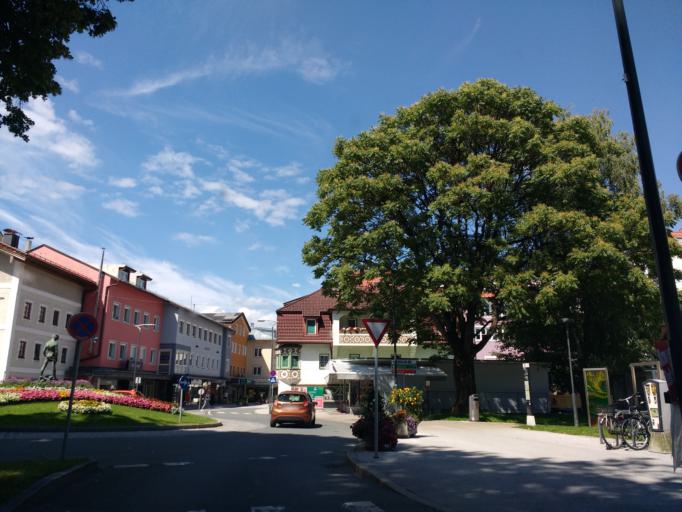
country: AT
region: Tyrol
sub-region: Politischer Bezirk Kufstein
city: Kufstein
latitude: 47.5842
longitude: 12.1715
